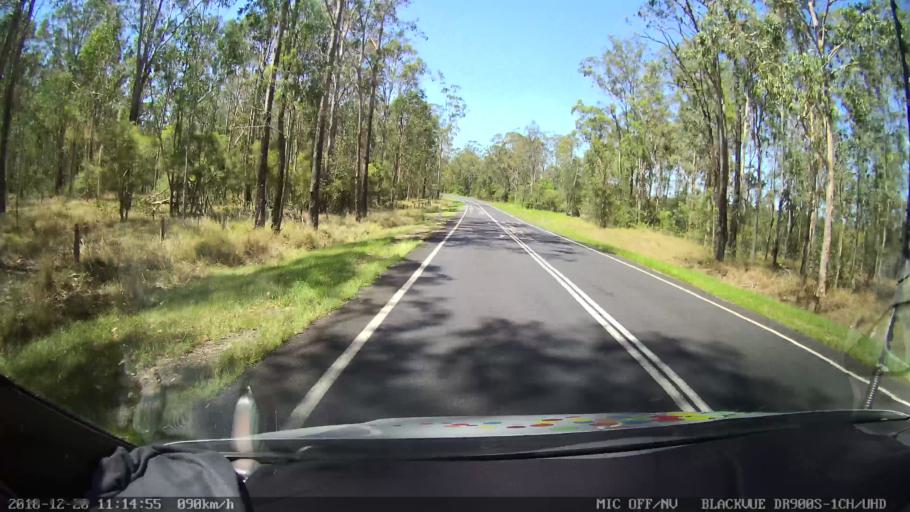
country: AU
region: New South Wales
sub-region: Richmond Valley
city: Casino
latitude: -29.0065
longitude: 153.0069
